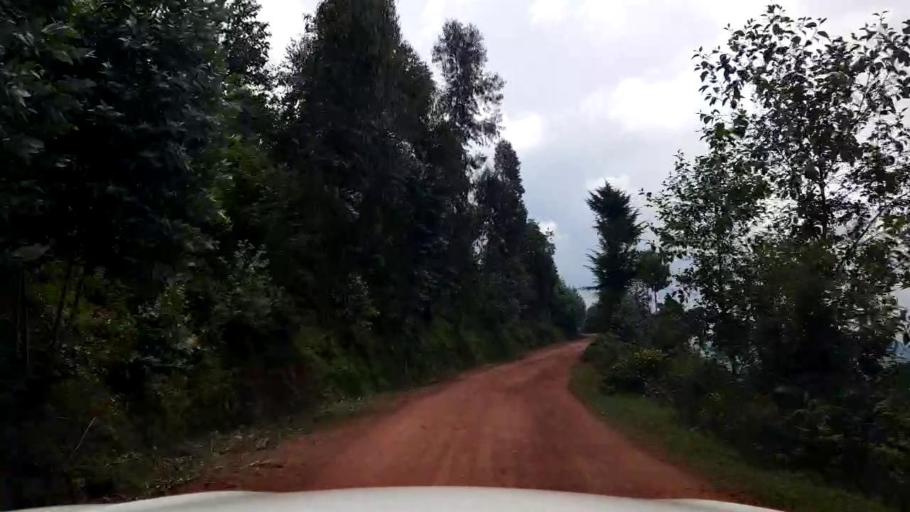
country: RW
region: Northern Province
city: Byumba
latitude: -1.4876
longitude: 29.9296
